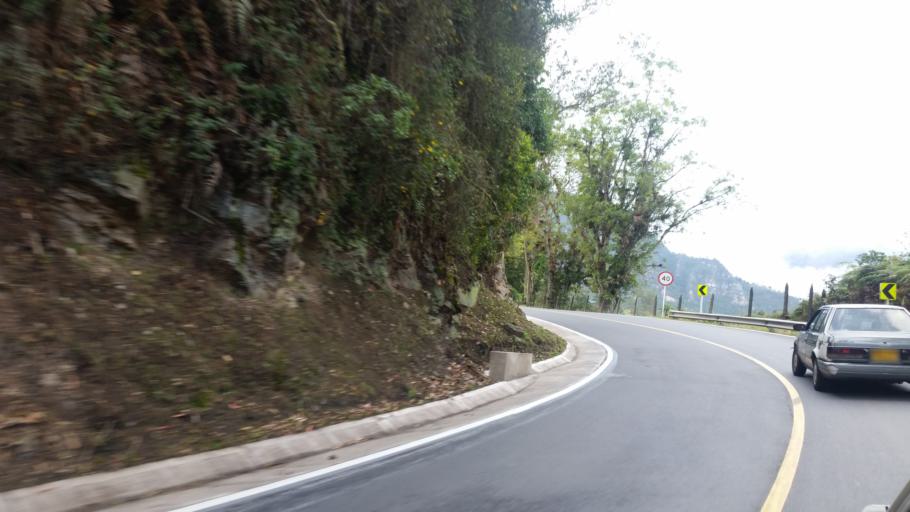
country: CO
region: Cundinamarca
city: Choachi
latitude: 4.5543
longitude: -73.9447
